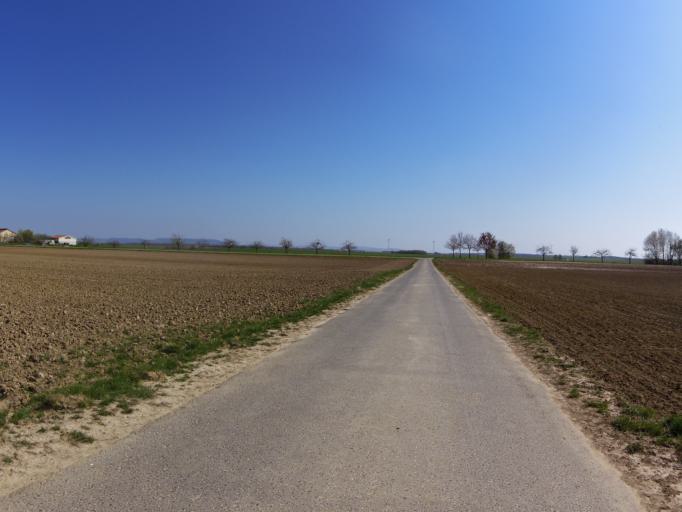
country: DE
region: Bavaria
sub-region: Regierungsbezirk Unterfranken
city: Biebelried
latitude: 49.8195
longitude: 10.0922
